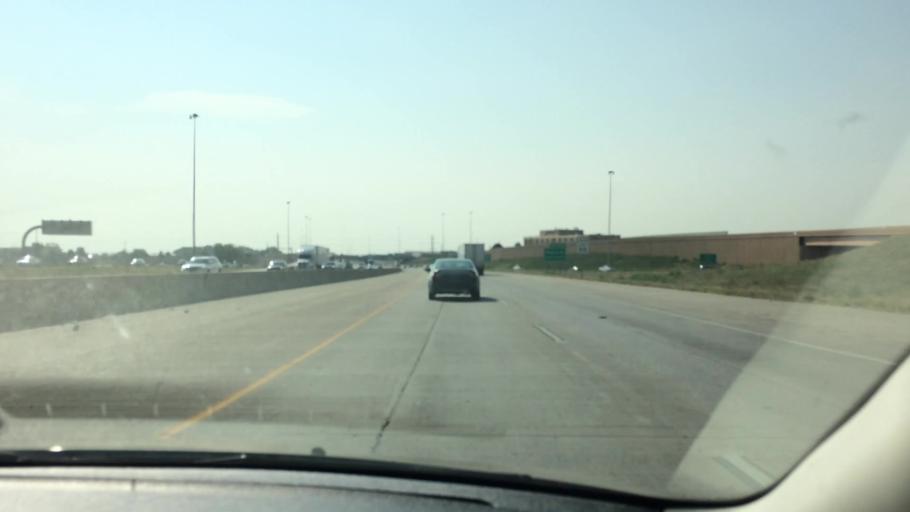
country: US
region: Colorado
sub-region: Adams County
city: Aurora
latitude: 39.7692
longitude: -104.8018
